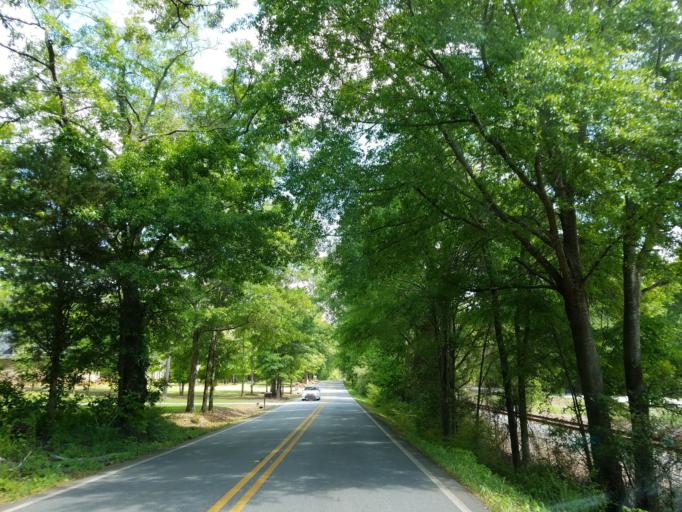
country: US
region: Georgia
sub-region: Bibb County
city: West Point
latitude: 32.9451
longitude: -83.7959
